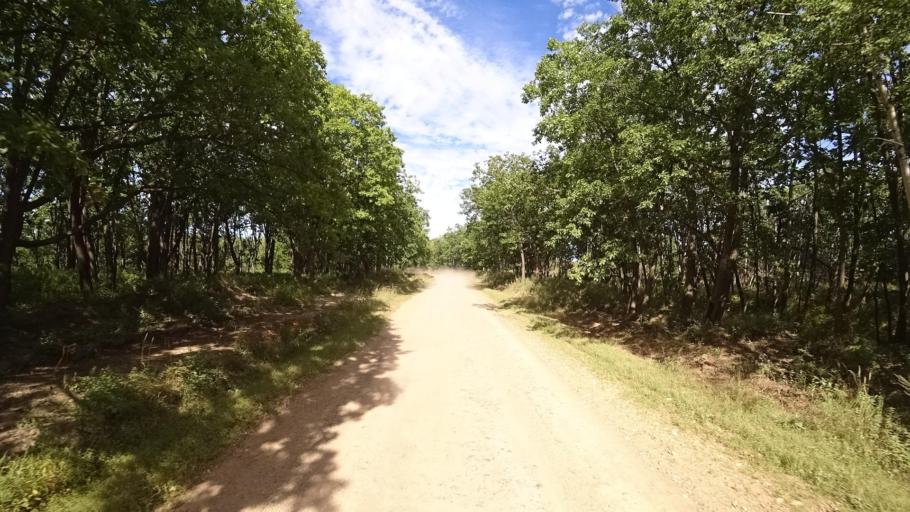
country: RU
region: Primorskiy
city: Yakovlevka
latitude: 44.4022
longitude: 133.5646
